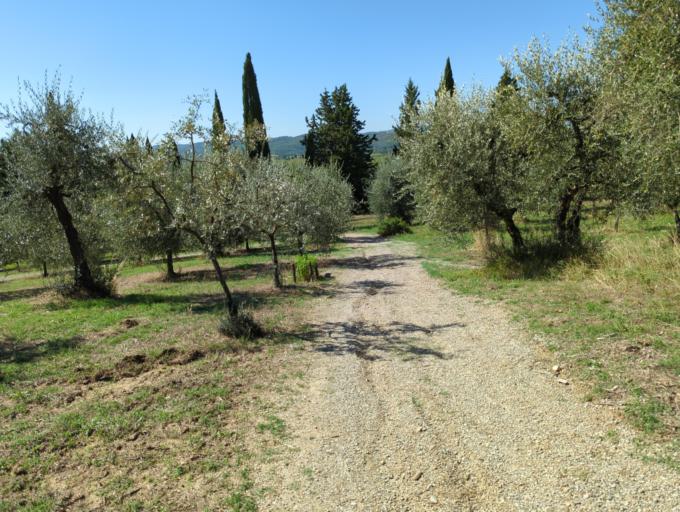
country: IT
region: Tuscany
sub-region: Province of Arezzo
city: Castiglion Fibocchi
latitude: 43.5278
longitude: 11.7815
